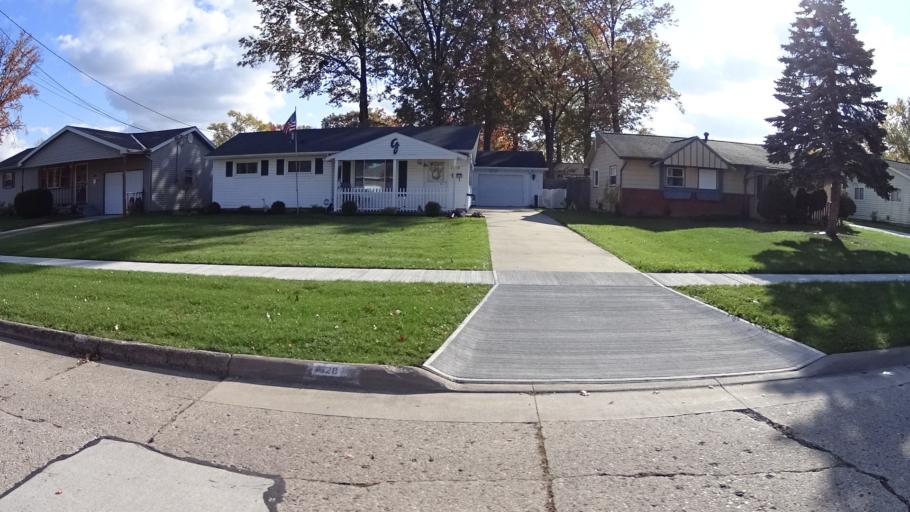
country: US
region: Ohio
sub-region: Lorain County
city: Sheffield
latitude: 41.4368
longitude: -82.1304
